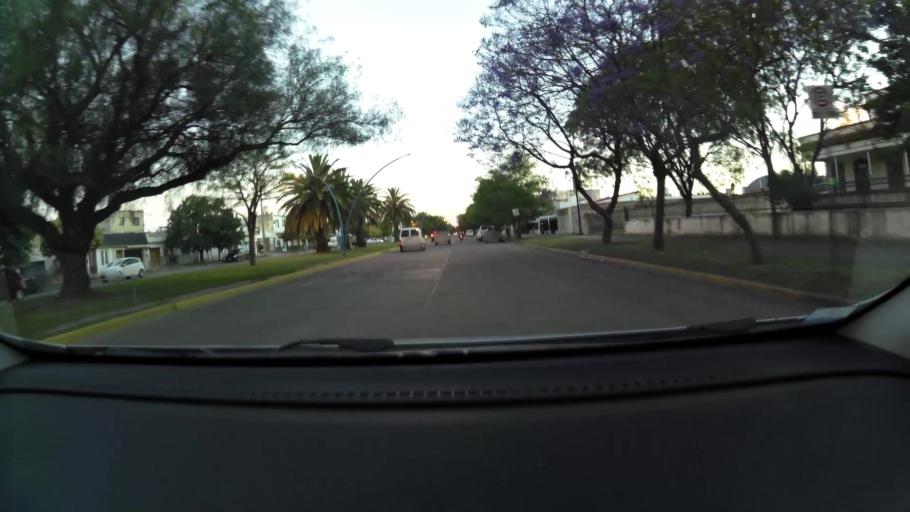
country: AR
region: Cordoba
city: Villa Maria
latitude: -32.4171
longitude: -63.2498
